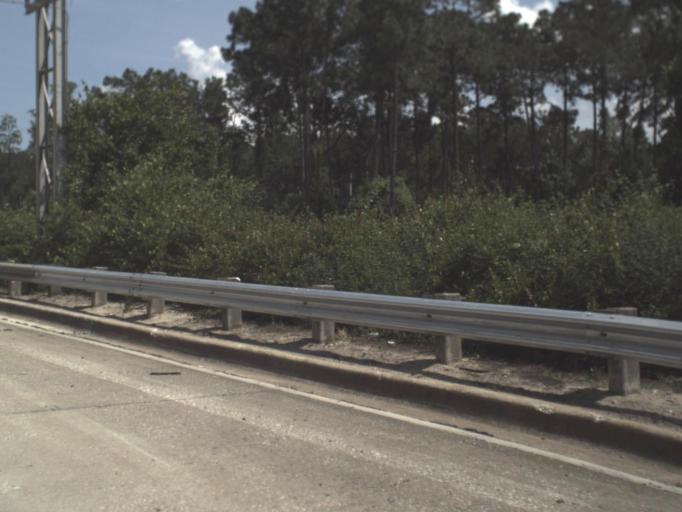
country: US
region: Florida
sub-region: Duval County
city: Jacksonville
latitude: 30.4593
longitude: -81.6489
